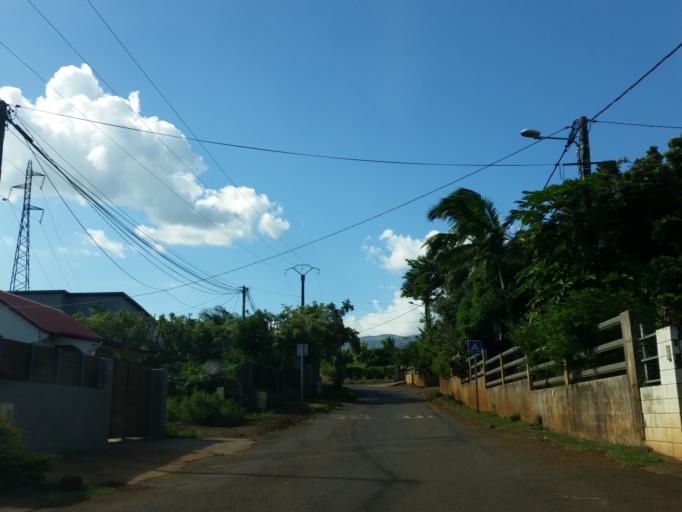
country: RE
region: Reunion
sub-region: Reunion
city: Saint-Pierre
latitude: -21.3255
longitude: 55.4987
